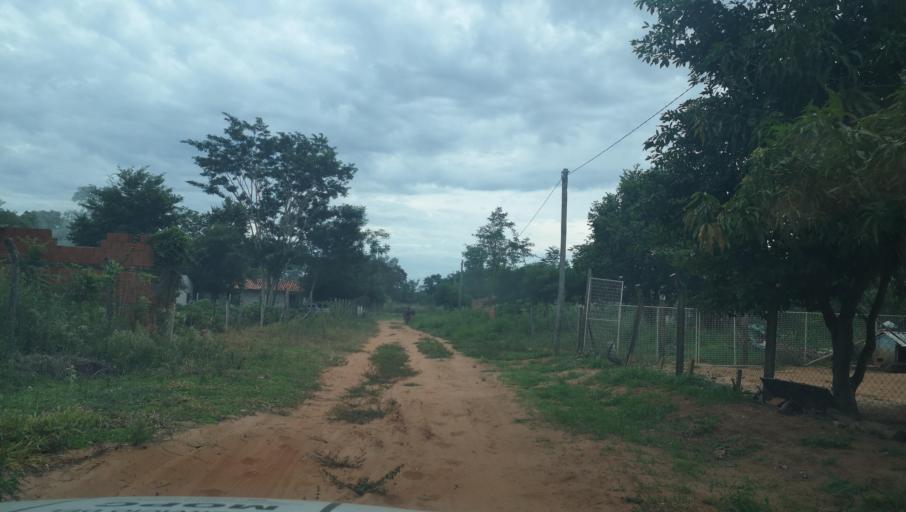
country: PY
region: San Pedro
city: Capiibary
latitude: -24.7446
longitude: -56.0287
